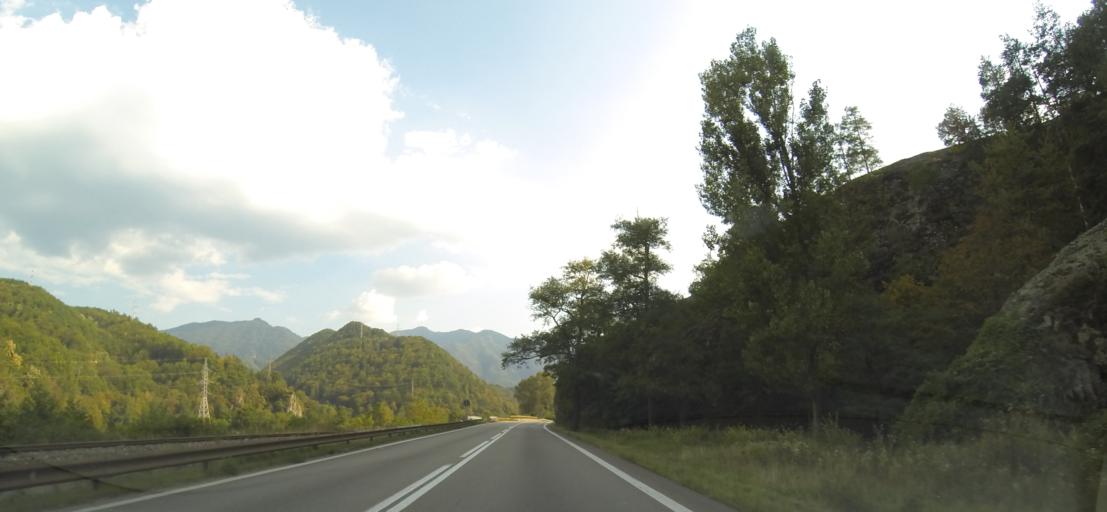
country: RO
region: Valcea
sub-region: Comuna Racovita
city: Racovita
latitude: 45.3780
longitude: 24.2954
